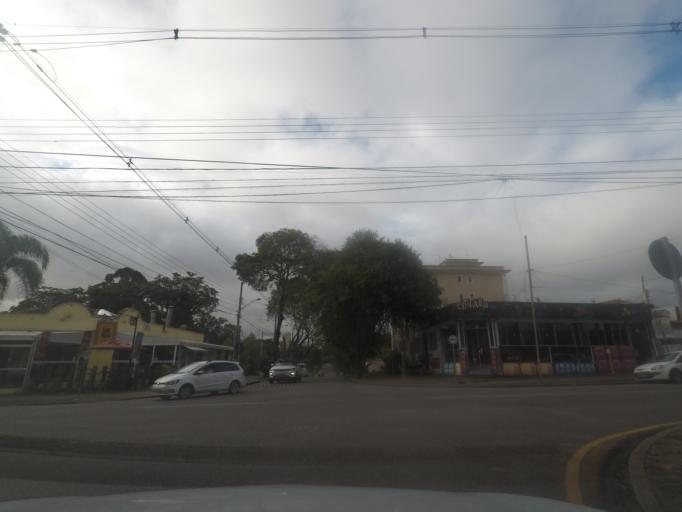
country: BR
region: Parana
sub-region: Curitiba
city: Curitiba
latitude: -25.4233
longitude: -49.2460
